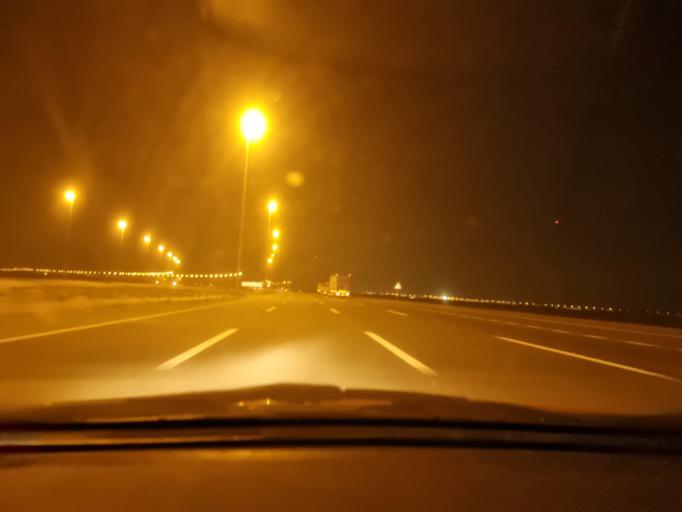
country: AE
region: Abu Dhabi
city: Abu Dhabi
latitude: 24.6042
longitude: 54.7549
